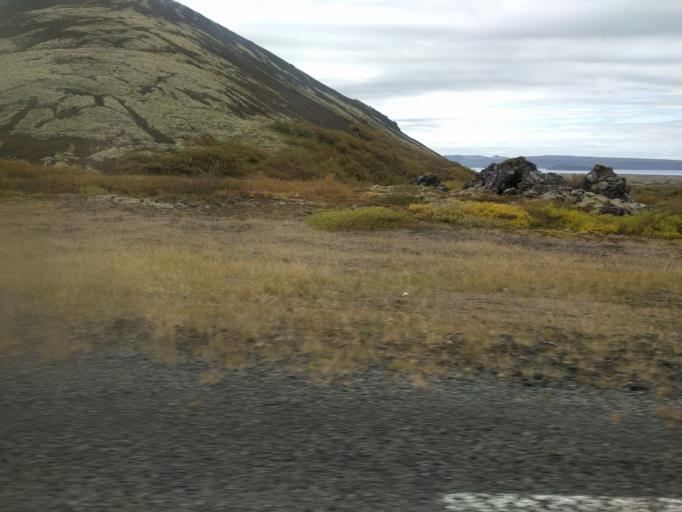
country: IS
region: South
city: Hveragerdi
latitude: 64.1982
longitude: -21.0301
